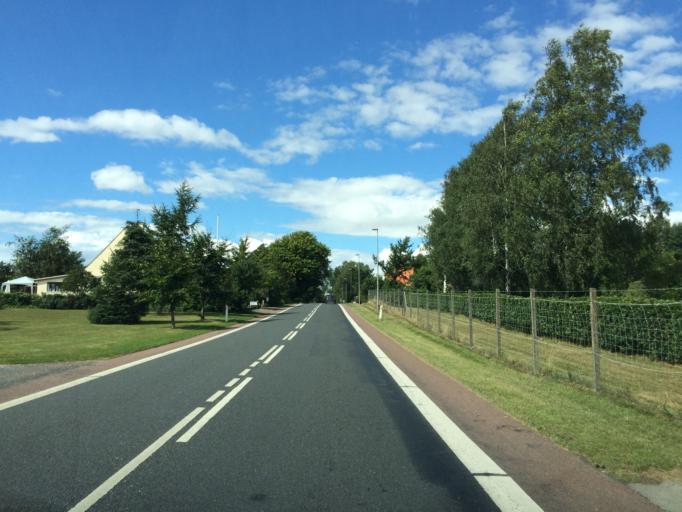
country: DK
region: South Denmark
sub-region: Assens Kommune
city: Harby
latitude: 55.1410
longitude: 10.1627
